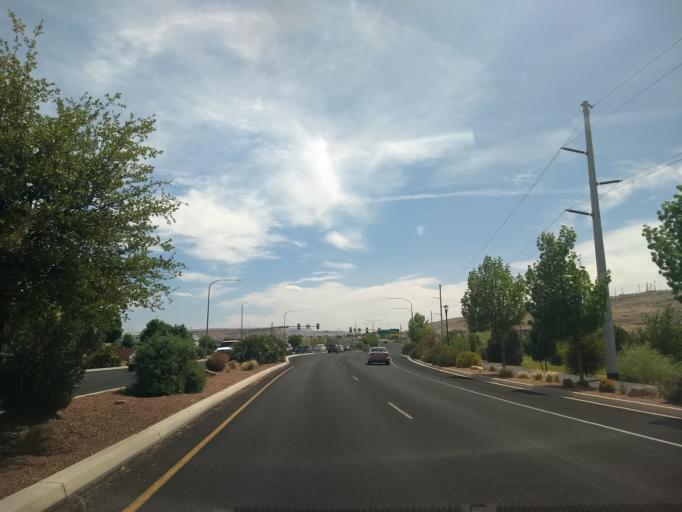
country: US
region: Utah
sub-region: Washington County
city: Saint George
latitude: 37.0762
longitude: -113.5901
